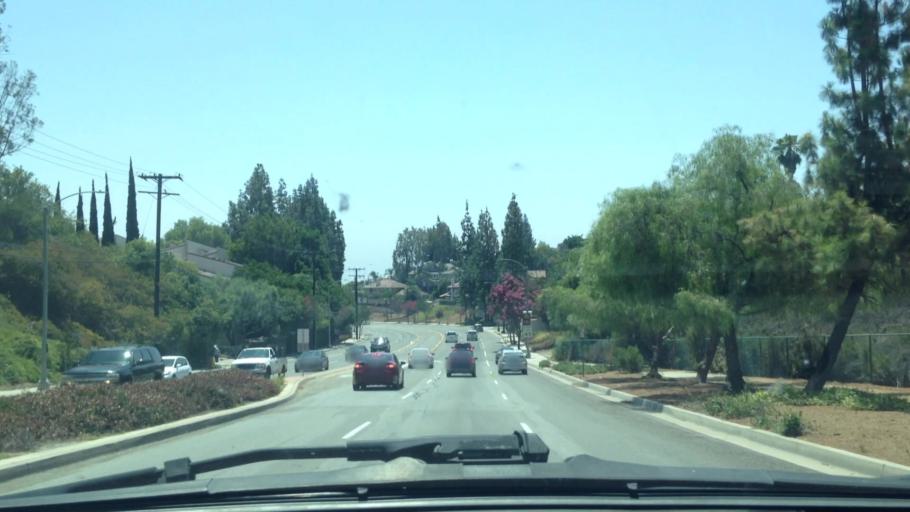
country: US
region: California
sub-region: Orange County
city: Brea
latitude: 33.8933
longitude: -117.8916
